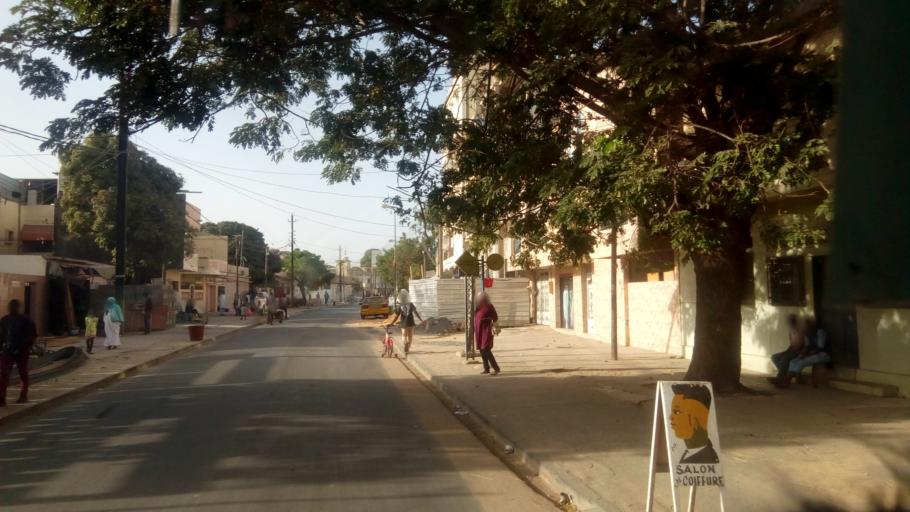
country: SN
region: Dakar
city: Grand Dakar
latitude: 14.7071
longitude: -17.4491
